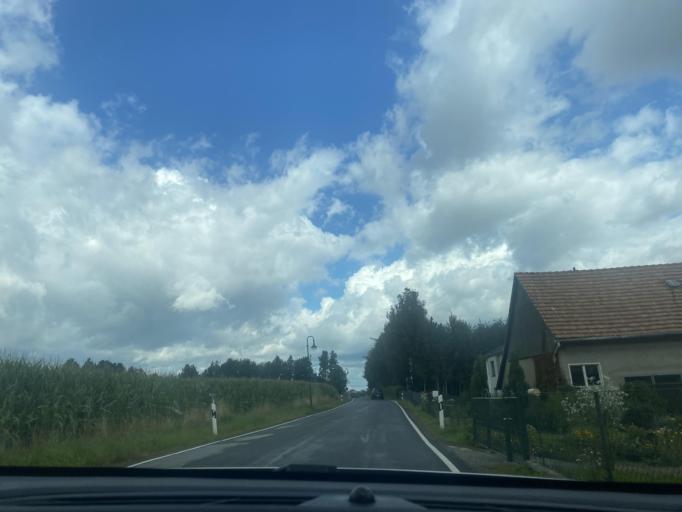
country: DE
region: Saxony
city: Sohland am Rotstein
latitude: 51.1320
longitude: 14.7729
